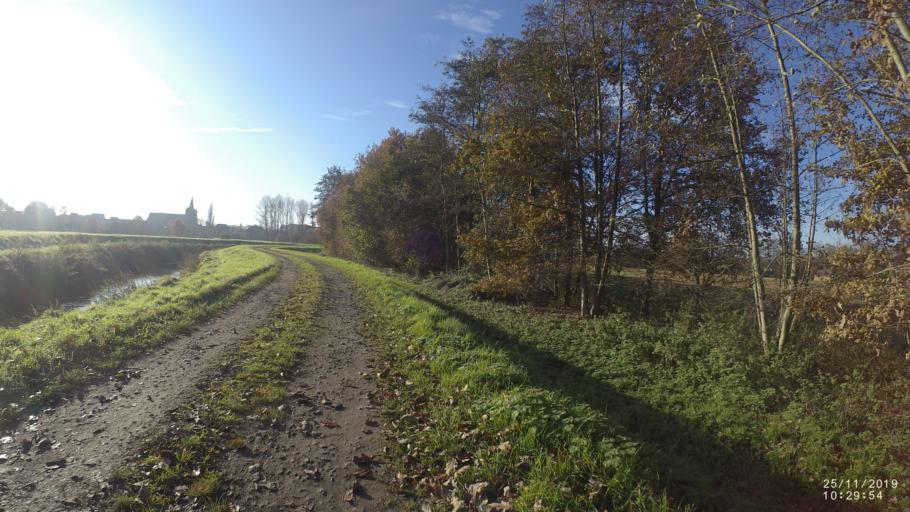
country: BE
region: Flanders
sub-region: Provincie Vlaams-Brabant
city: Scherpenheuvel-Zichem
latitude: 51.0055
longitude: 4.9839
